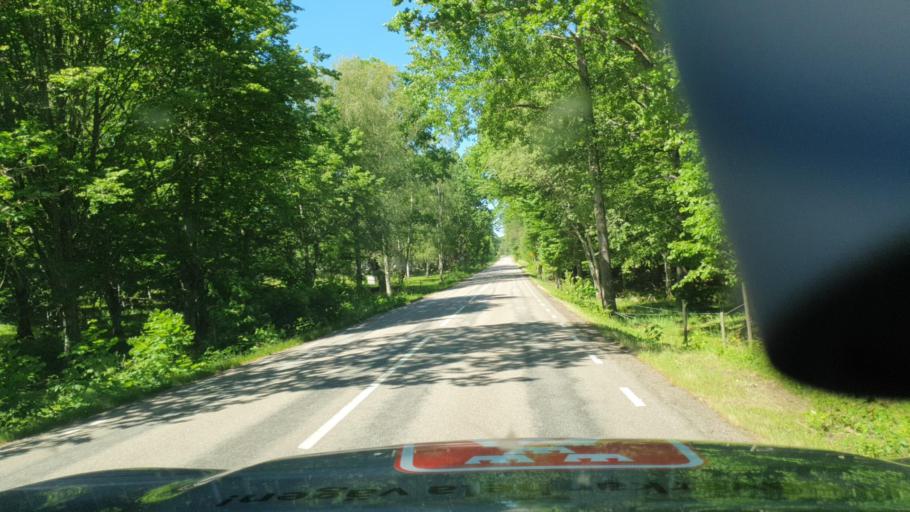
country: SE
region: Kalmar
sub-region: Torsas Kommun
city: Torsas
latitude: 56.4836
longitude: 15.7519
